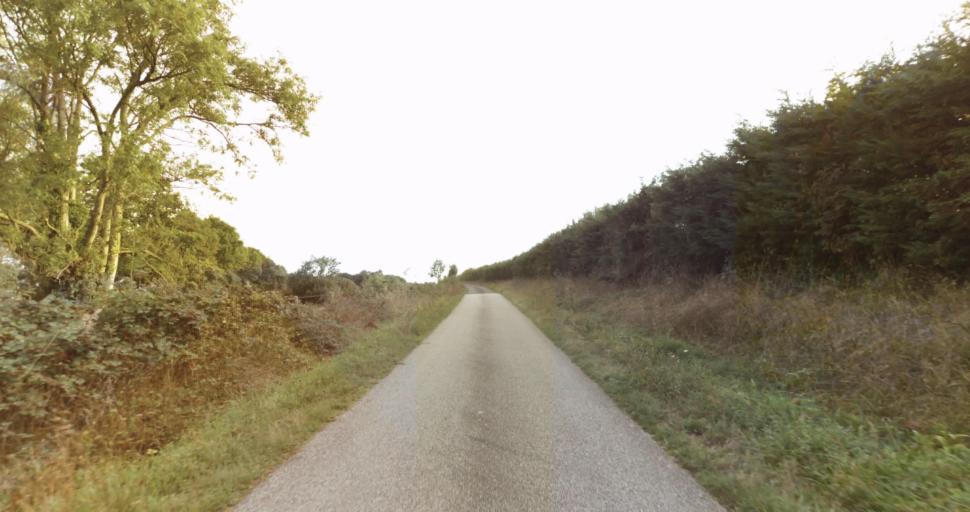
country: FR
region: Lower Normandy
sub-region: Departement de l'Orne
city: Gace
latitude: 48.7476
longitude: 0.2727
